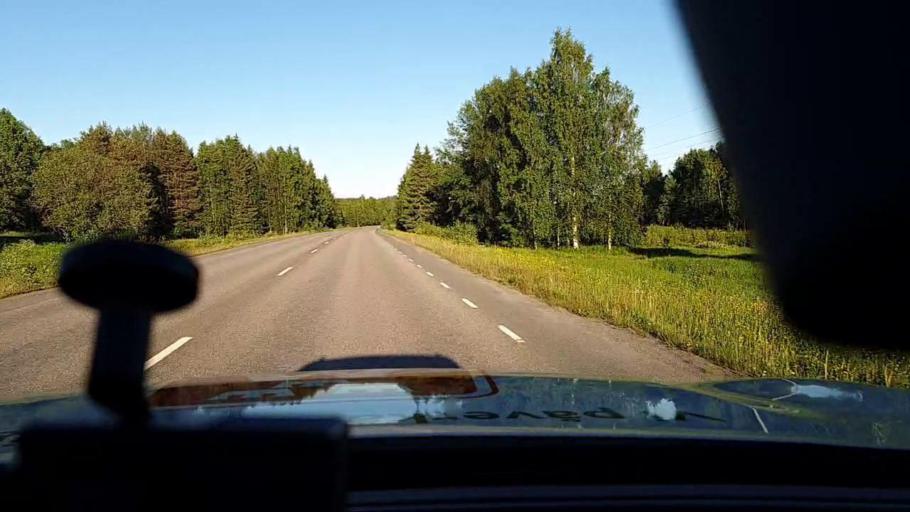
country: SE
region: Norrbotten
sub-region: Lulea Kommun
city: Lulea
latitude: 65.6142
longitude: 22.1538
